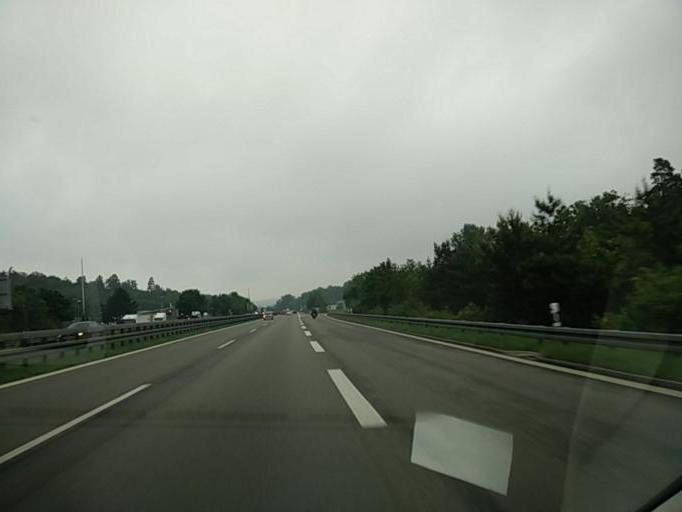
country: DE
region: Baden-Wuerttemberg
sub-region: Regierungsbezirk Stuttgart
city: Nufringen
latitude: 48.6126
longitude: 8.9024
